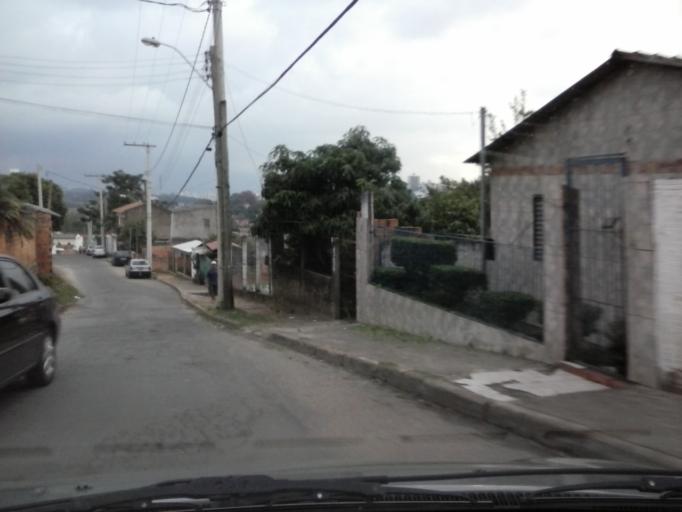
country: BR
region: Rio Grande do Sul
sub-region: Porto Alegre
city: Porto Alegre
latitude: -30.0501
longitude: -51.1544
